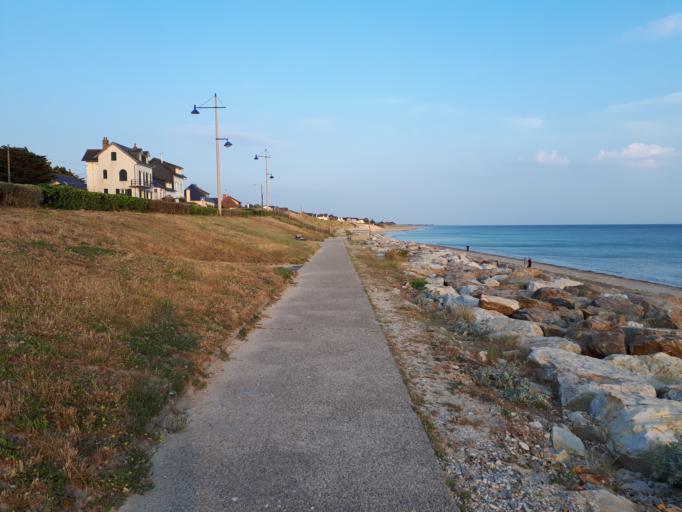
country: FR
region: Lower Normandy
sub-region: Departement de la Manche
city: Barneville-Plage
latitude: 49.3657
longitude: -1.7686
